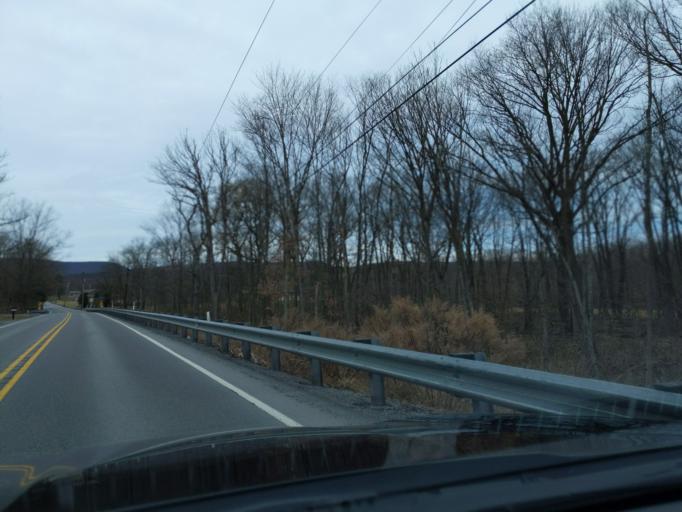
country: US
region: Pennsylvania
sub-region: Blair County
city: Greenwood
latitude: 40.5574
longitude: -78.3764
